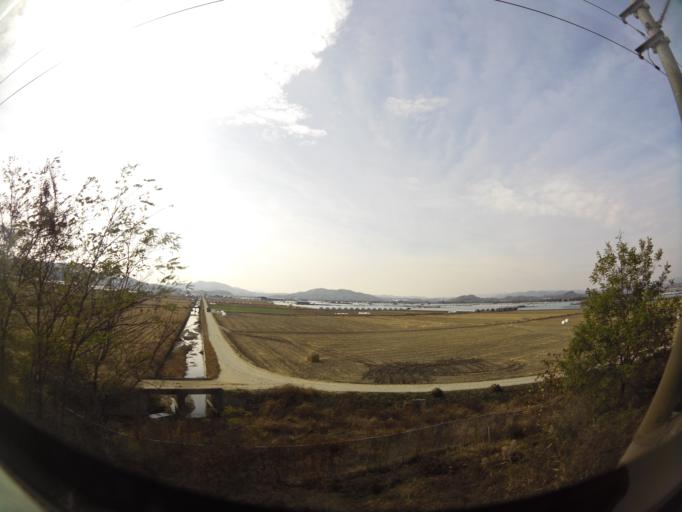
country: KR
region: Daejeon
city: Songgang-dong
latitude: 36.5645
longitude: 127.3196
